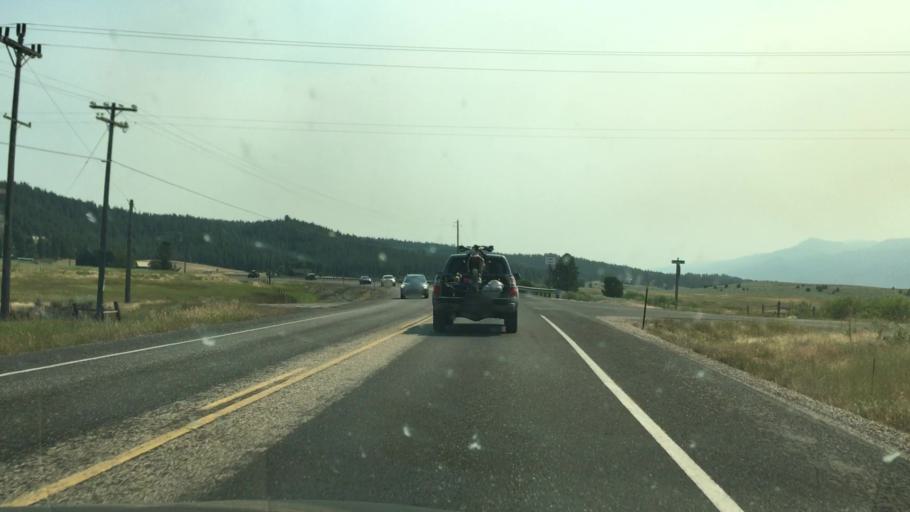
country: US
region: Idaho
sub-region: Valley County
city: Cascade
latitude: 44.6005
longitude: -116.0485
